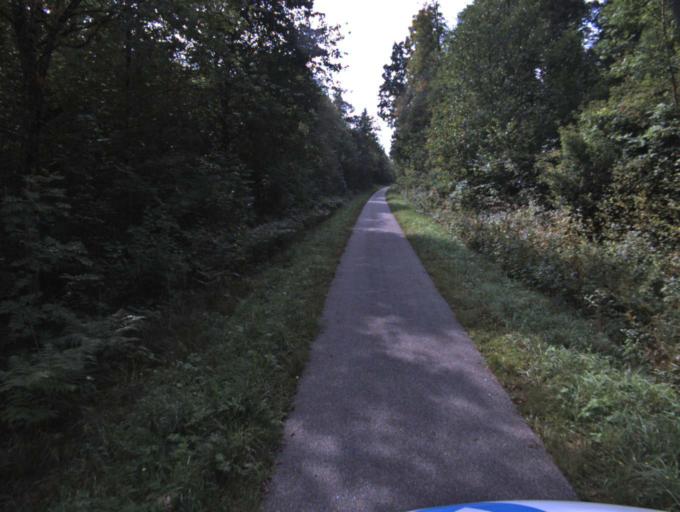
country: SE
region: Vaestra Goetaland
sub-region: Tranemo Kommun
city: Limmared
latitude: 57.6582
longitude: 13.3626
